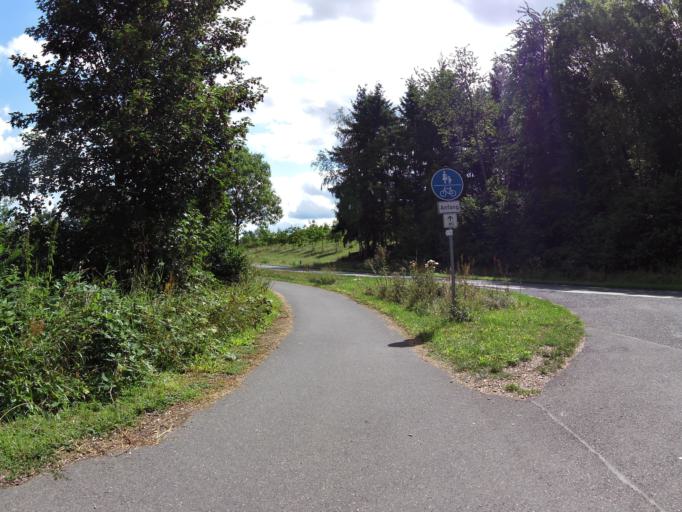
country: DE
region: Bavaria
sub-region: Regierungsbezirk Unterfranken
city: Volkach
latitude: 49.8537
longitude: 10.2206
